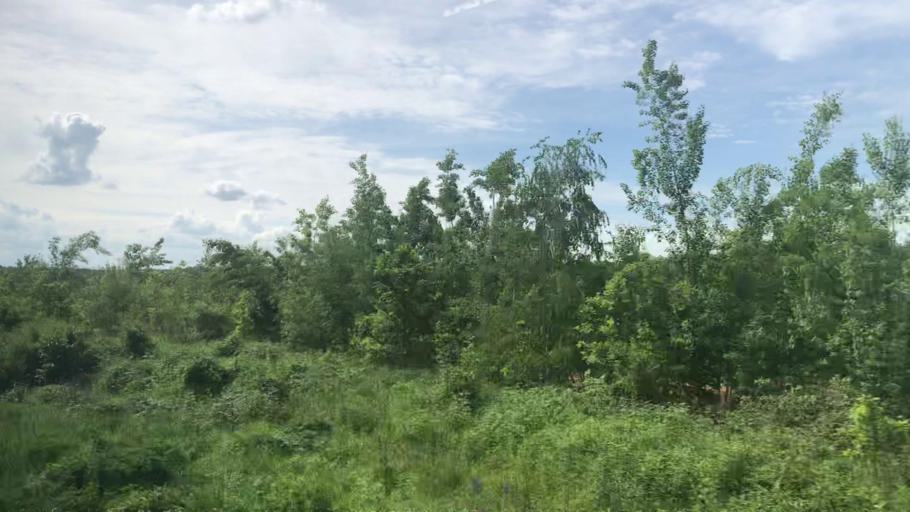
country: PL
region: Lower Silesian Voivodeship
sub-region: Powiat wroclawski
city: Katy Wroclawskie
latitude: 50.9957
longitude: 16.6810
